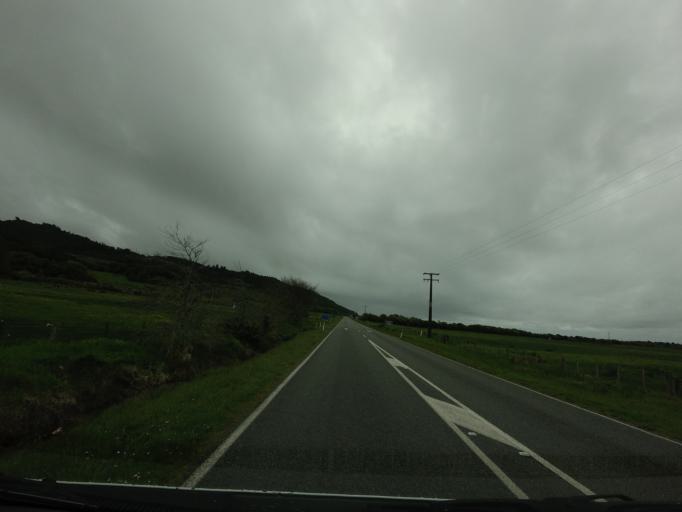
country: NZ
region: West Coast
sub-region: Westland District
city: Hokitika
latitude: -42.8934
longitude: 170.8095
